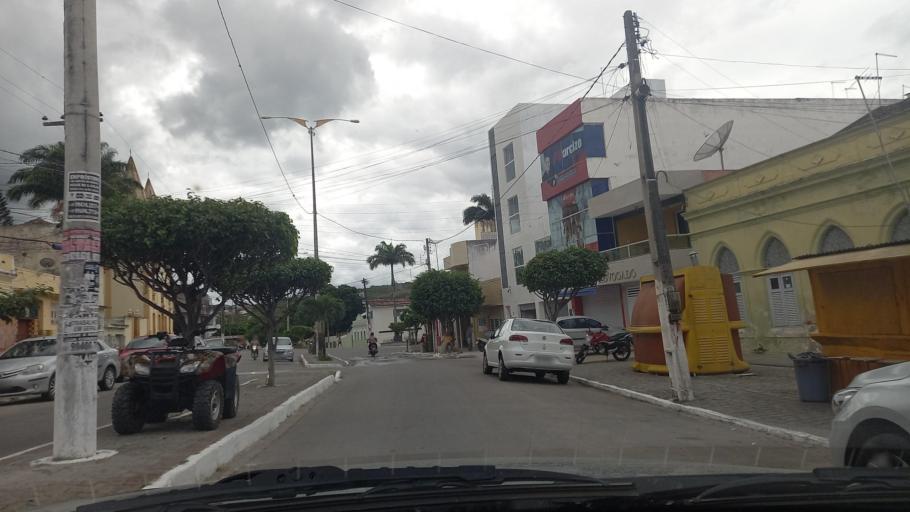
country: BR
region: Pernambuco
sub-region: Caruaru
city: Caruaru
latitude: -8.3260
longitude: -36.1377
